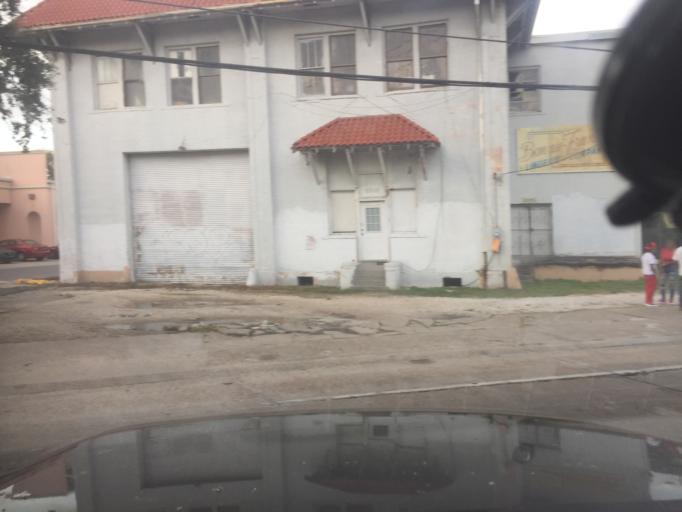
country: US
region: Louisiana
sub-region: Orleans Parish
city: New Orleans
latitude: 29.9891
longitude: -90.0735
